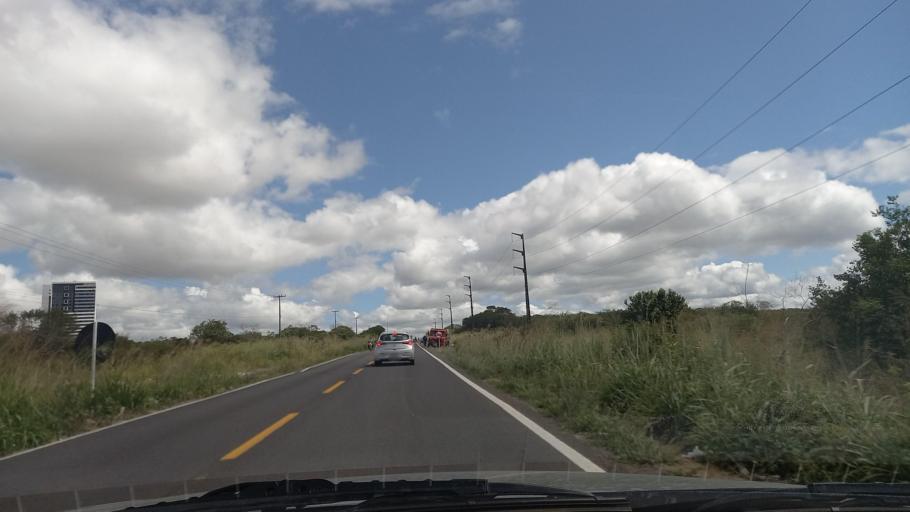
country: BR
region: Pernambuco
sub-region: Caruaru
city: Caruaru
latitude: -8.2566
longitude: -35.9598
